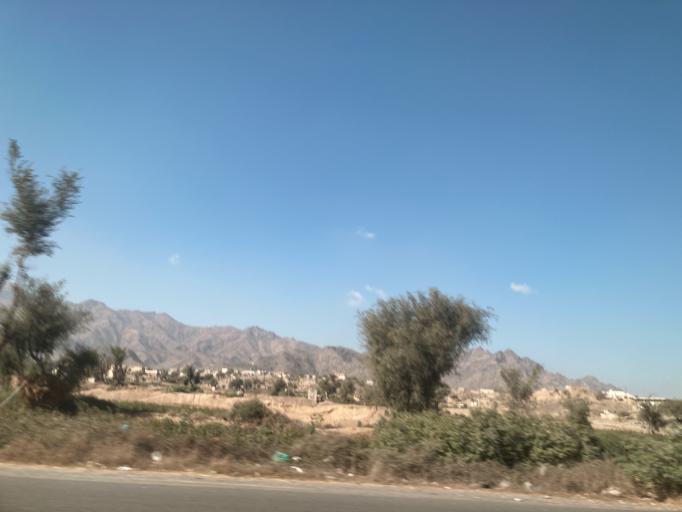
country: YE
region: Ad Dali'
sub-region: Al Hussein
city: Al Husayn
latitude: 13.7968
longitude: 44.7285
